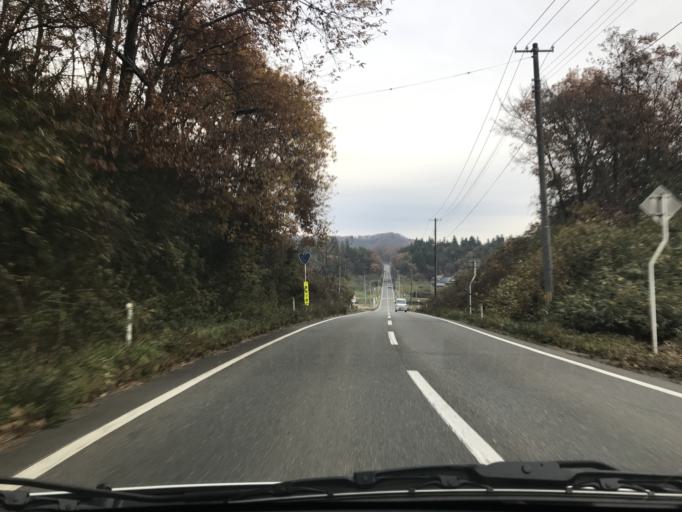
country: JP
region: Iwate
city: Kitakami
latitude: 39.2877
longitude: 141.2221
